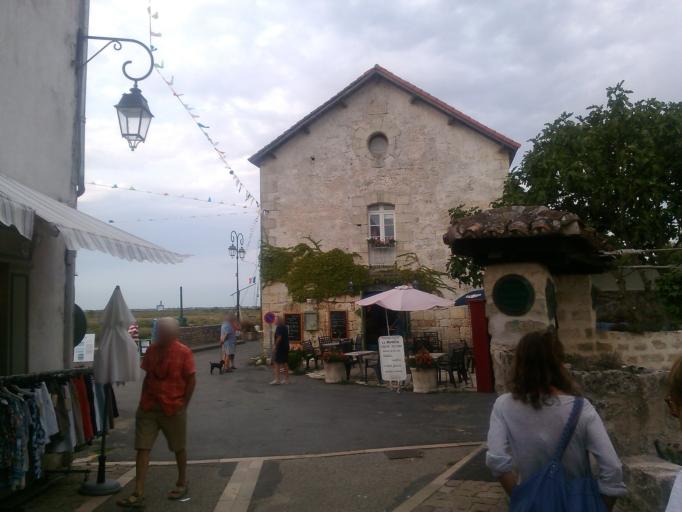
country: FR
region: Poitou-Charentes
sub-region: Departement de la Charente-Maritime
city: Breuillet
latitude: 45.7110
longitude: -1.0272
